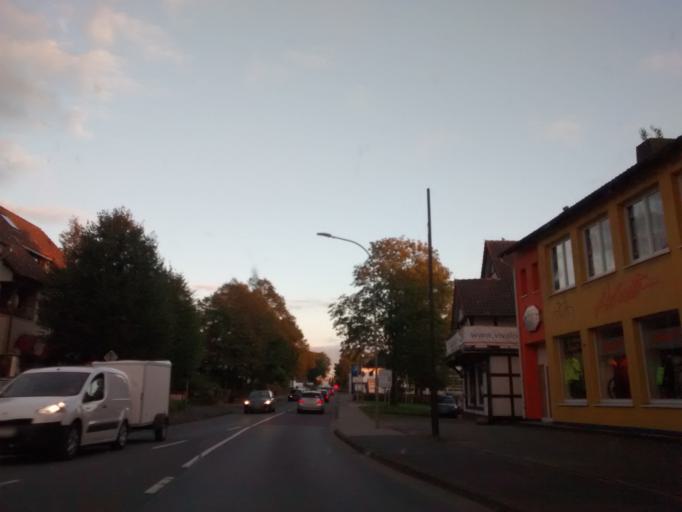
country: DE
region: North Rhine-Westphalia
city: Halle
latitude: 52.0596
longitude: 8.3645
